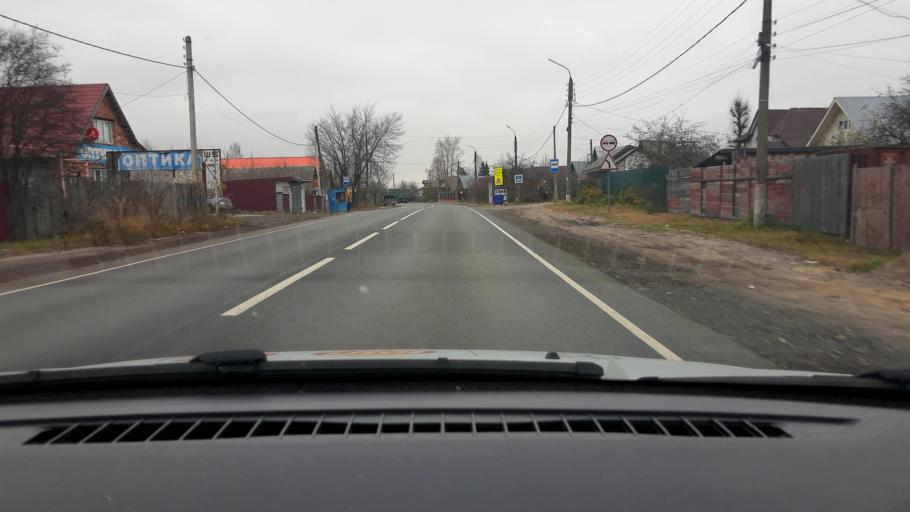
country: RU
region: Nizjnij Novgorod
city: Gidrotorf
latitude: 56.5371
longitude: 43.5371
